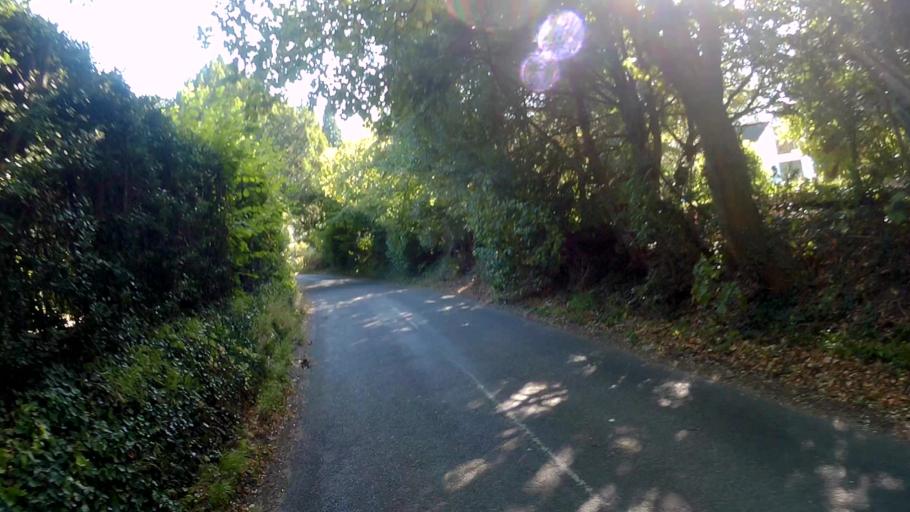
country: GB
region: England
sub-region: Surrey
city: Churt
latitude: 51.1704
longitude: -0.8004
